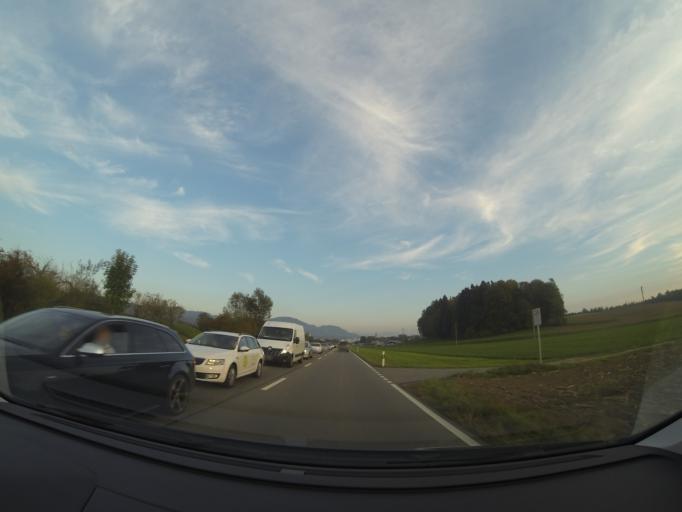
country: CH
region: Zurich
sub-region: Bezirk Hinwil
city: Wetzikon / Unter-Wetzikon
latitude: 47.3119
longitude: 8.8054
